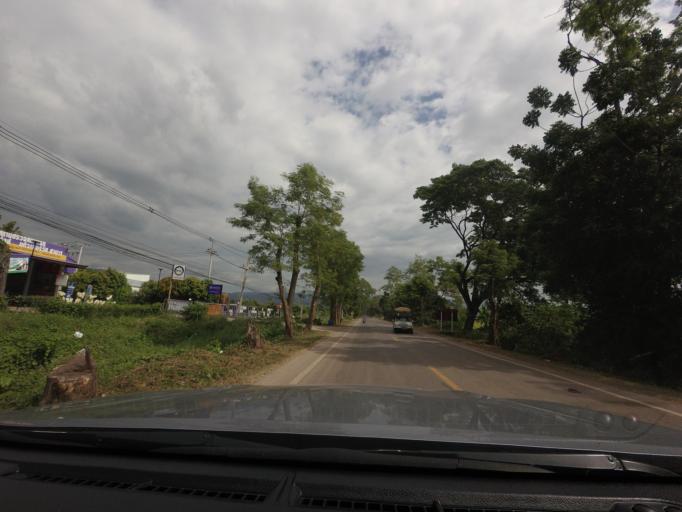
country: TH
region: Phitsanulok
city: Noen Maprang
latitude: 16.5693
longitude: 100.6460
